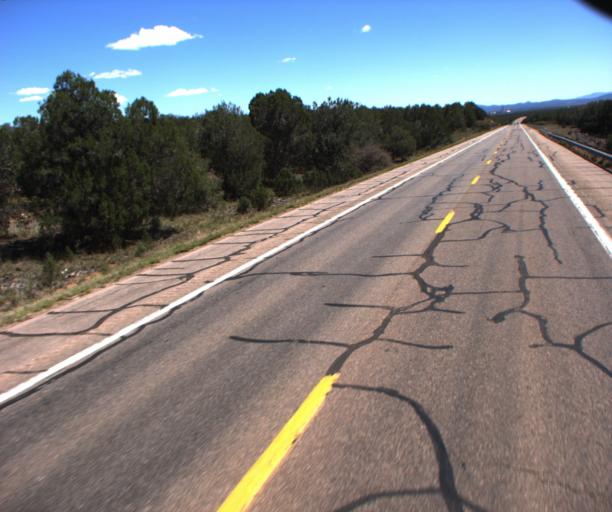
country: US
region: Arizona
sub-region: Yavapai County
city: Paulden
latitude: 35.0626
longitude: -112.3994
